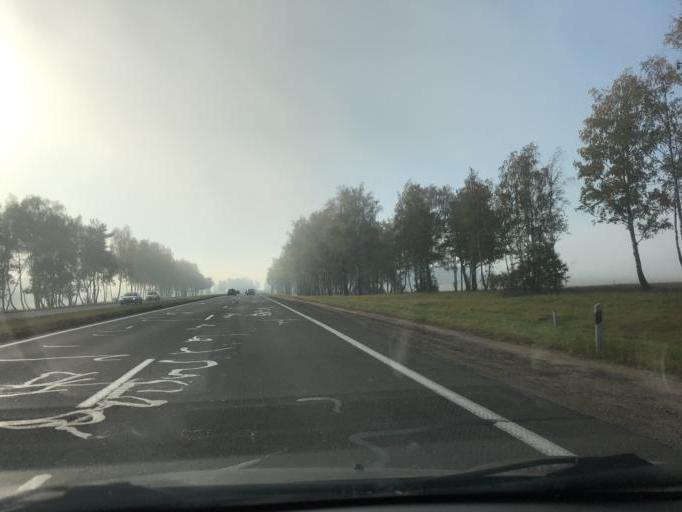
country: BY
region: Minsk
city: Luhavaya Slabada
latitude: 53.7821
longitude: 27.8236
